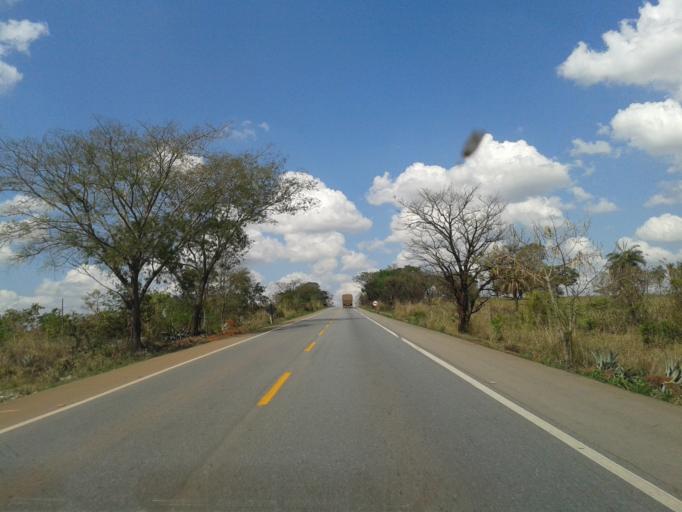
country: BR
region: Minas Gerais
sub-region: Luz
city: Luz
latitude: -19.7578
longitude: -45.8135
